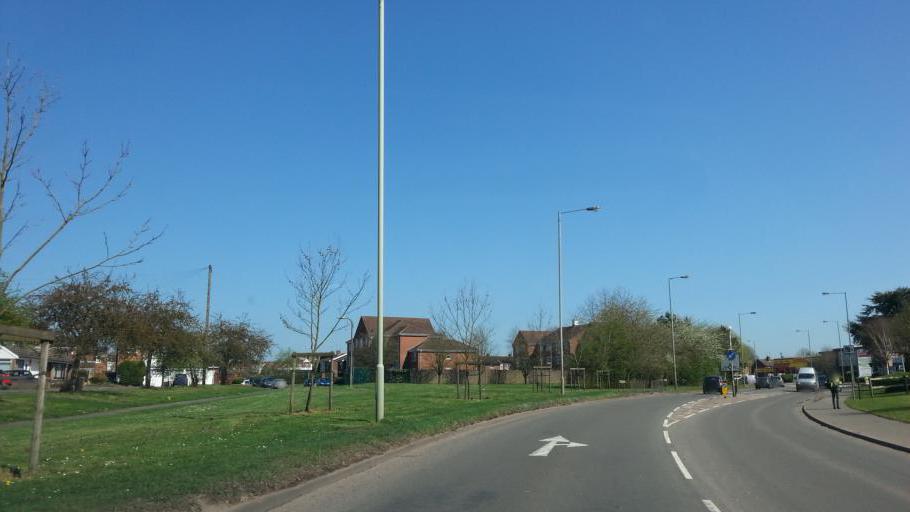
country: GB
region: England
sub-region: Staffordshire
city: Cannock
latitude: 52.6818
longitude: -2.0416
